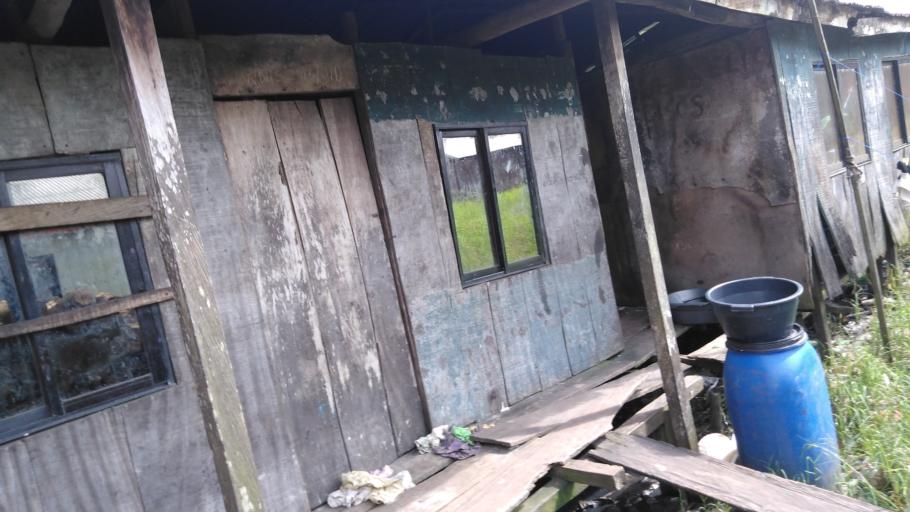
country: NG
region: Ondo
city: Igbekebo
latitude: 5.9216
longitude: 4.9665
